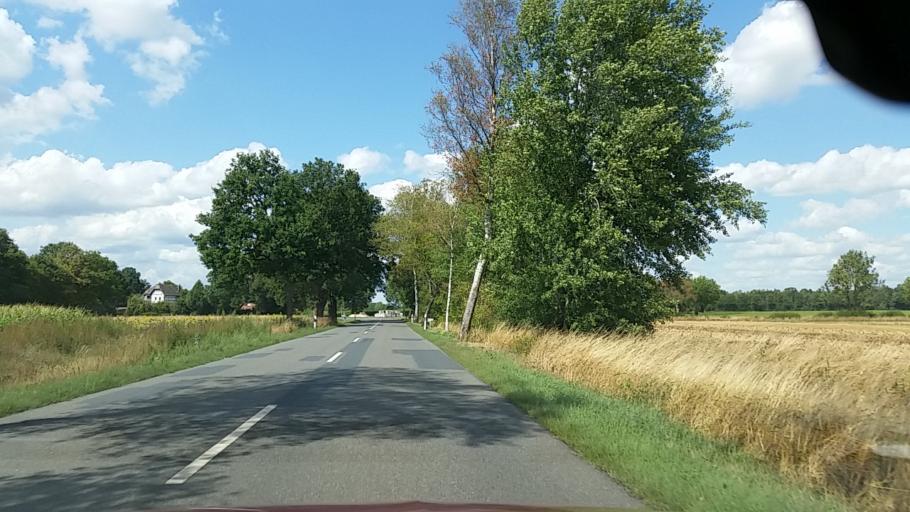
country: DE
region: Lower Saxony
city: Wittingen
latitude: 52.6971
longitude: 10.6727
